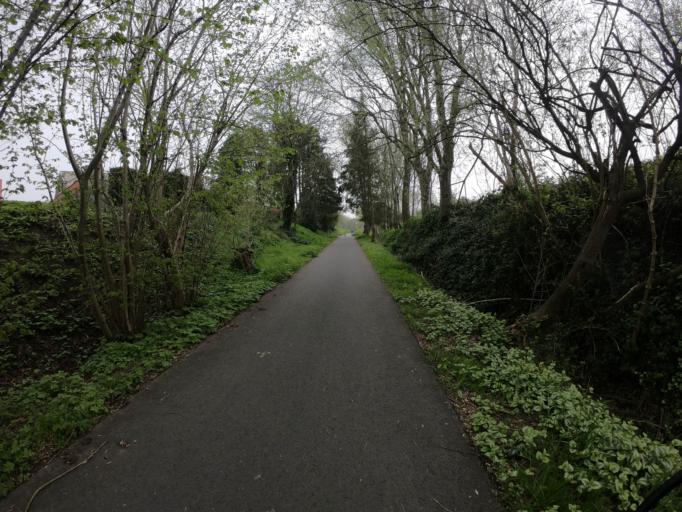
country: BE
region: Flanders
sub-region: Provincie West-Vlaanderen
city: Avelgem
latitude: 50.7731
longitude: 3.4335
